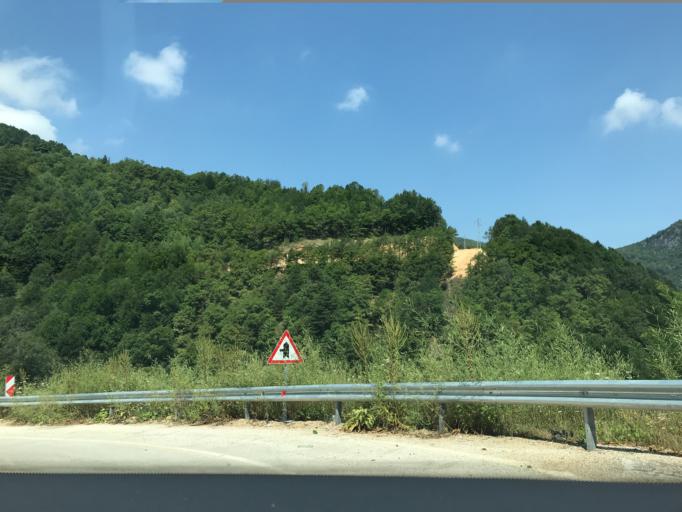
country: TR
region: Bursa
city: Tahtakopru
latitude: 39.9303
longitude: 29.5882
